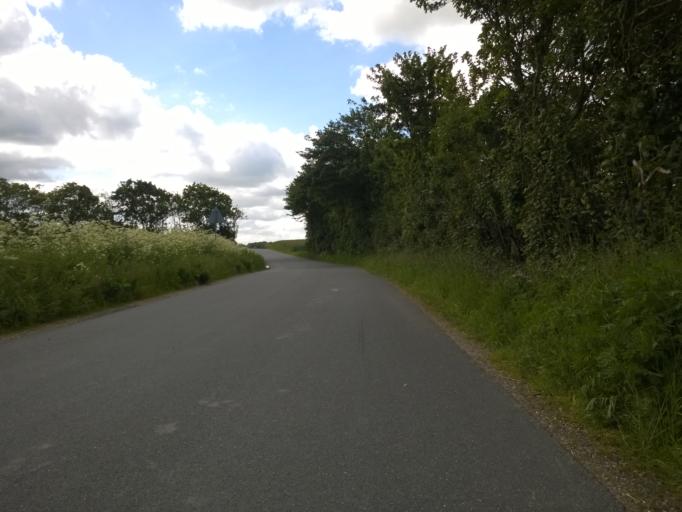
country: DK
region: Central Jutland
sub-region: Holstebro Kommune
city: Vinderup
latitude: 56.4040
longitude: 8.7759
